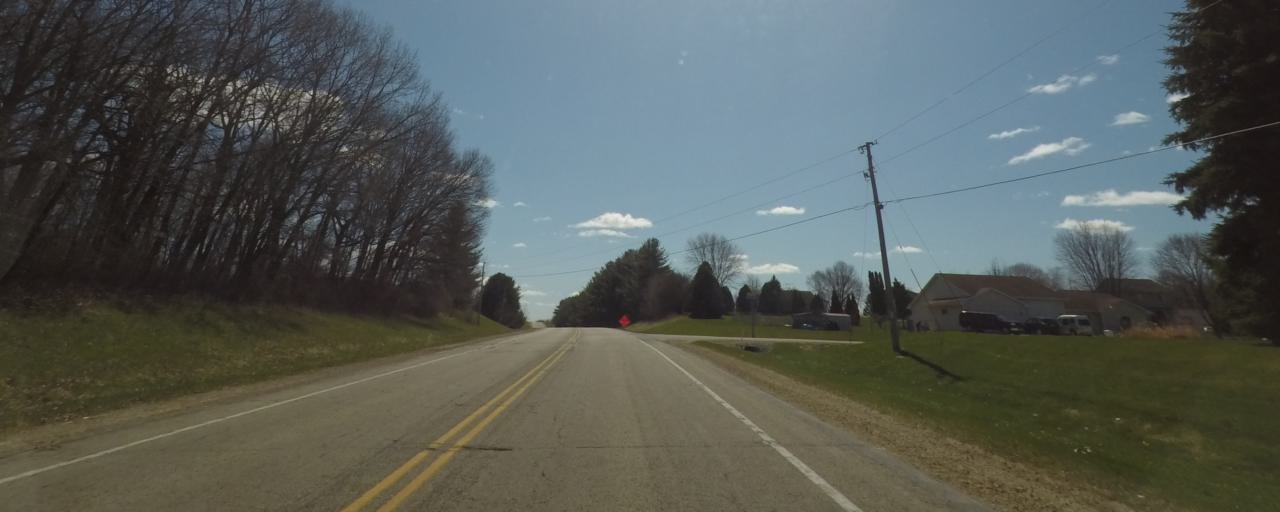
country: US
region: Wisconsin
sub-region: Dane County
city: Cottage Grove
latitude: 43.0824
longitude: -89.1600
